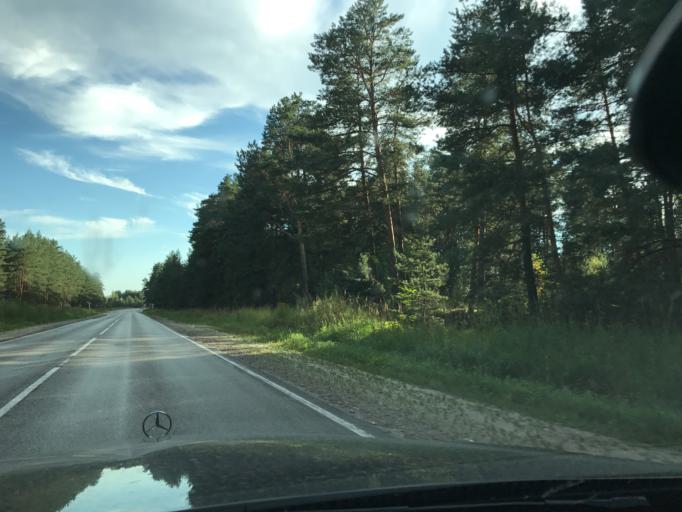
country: RU
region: Vladimir
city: Kommunar
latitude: 56.0430
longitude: 40.4325
